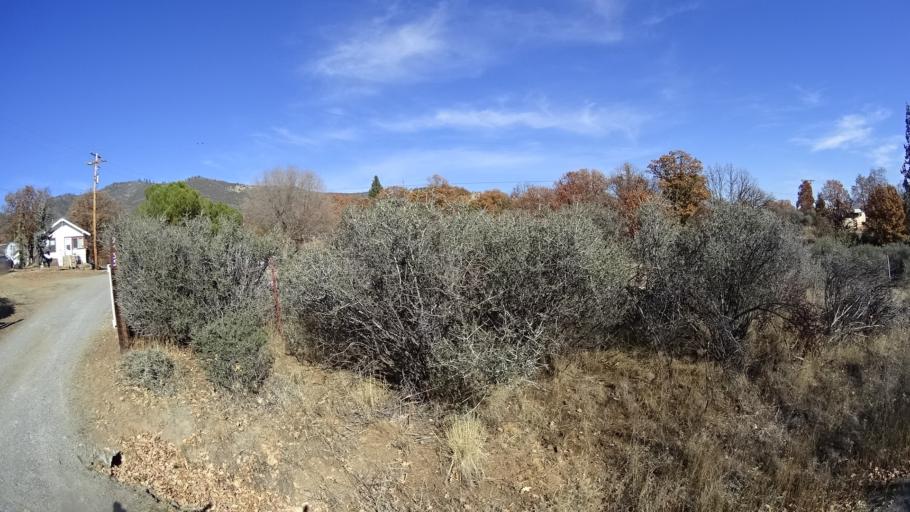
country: US
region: California
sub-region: Siskiyou County
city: Yreka
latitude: 41.7706
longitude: -122.6399
